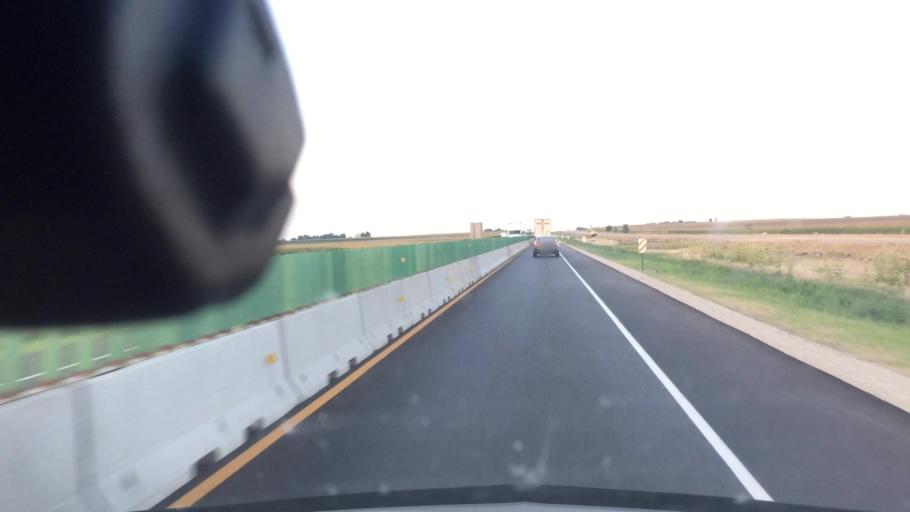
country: US
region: Illinois
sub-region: Livingston County
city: Pontiac
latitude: 40.9278
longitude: -88.6234
